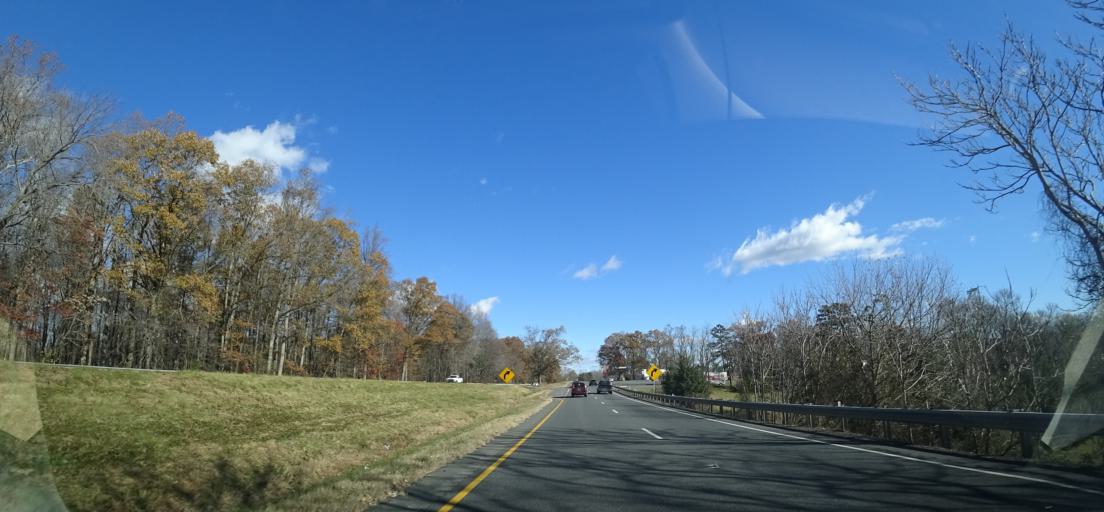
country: US
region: Virginia
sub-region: Madison County
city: Brightwood
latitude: 38.4156
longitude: -78.2063
